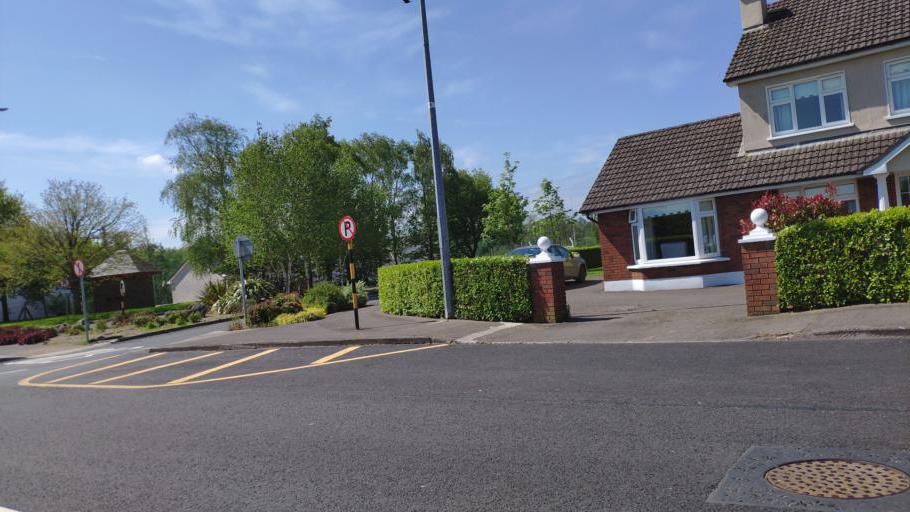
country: IE
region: Munster
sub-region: County Cork
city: Blarney
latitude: 51.9297
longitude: -8.5588
